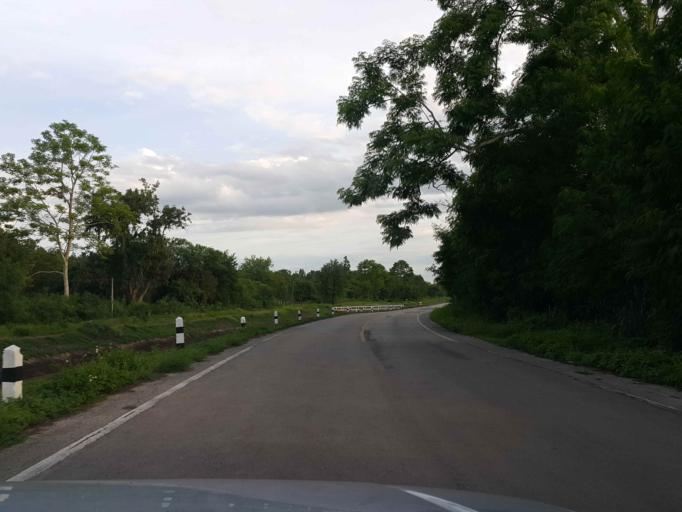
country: TH
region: Chiang Mai
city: San Sai
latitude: 18.9143
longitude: 99.1488
